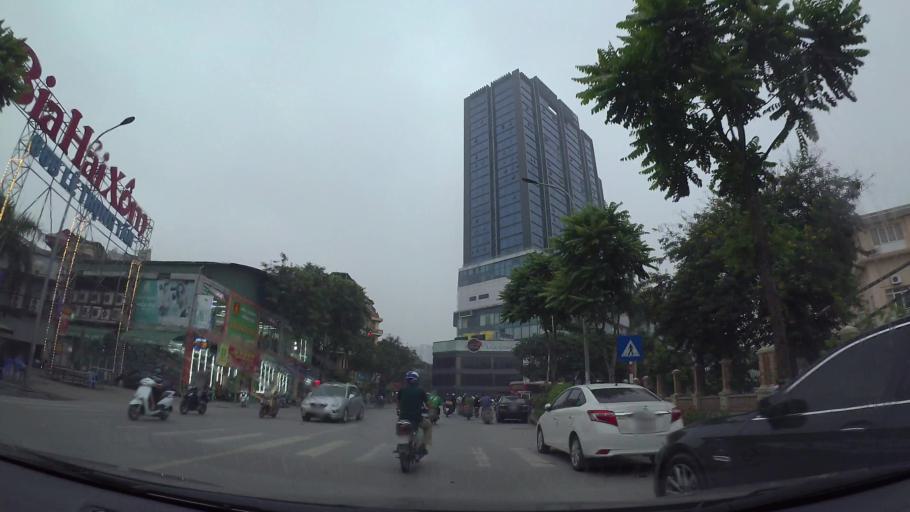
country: VN
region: Ha Noi
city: Dong Da
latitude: 20.9984
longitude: 105.8287
